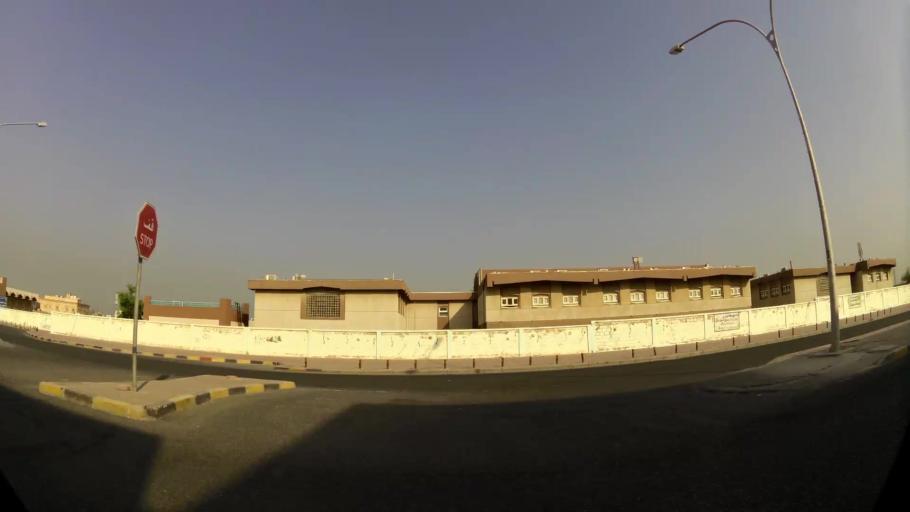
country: KW
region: Al Ahmadi
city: Al Manqaf
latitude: 29.1135
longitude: 48.1055
